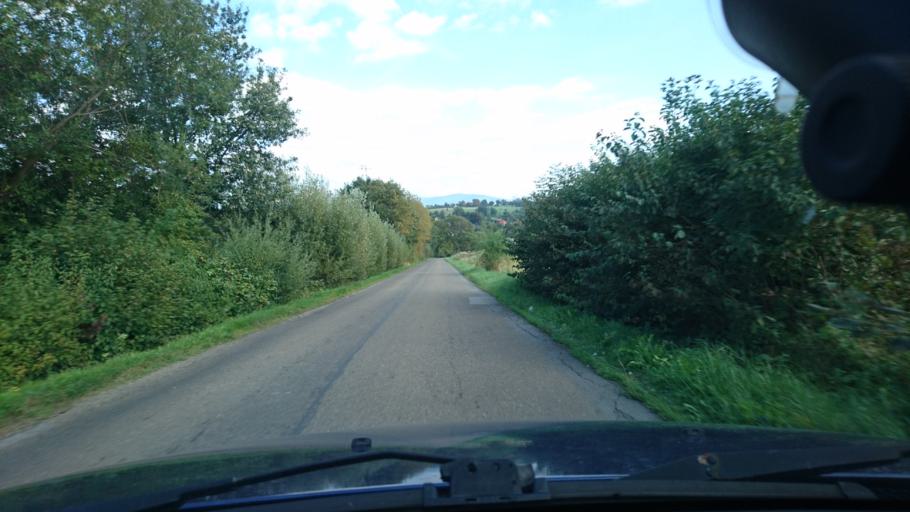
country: PL
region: Silesian Voivodeship
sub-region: Powiat bielski
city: Jasienica
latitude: 49.8313
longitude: 18.9361
